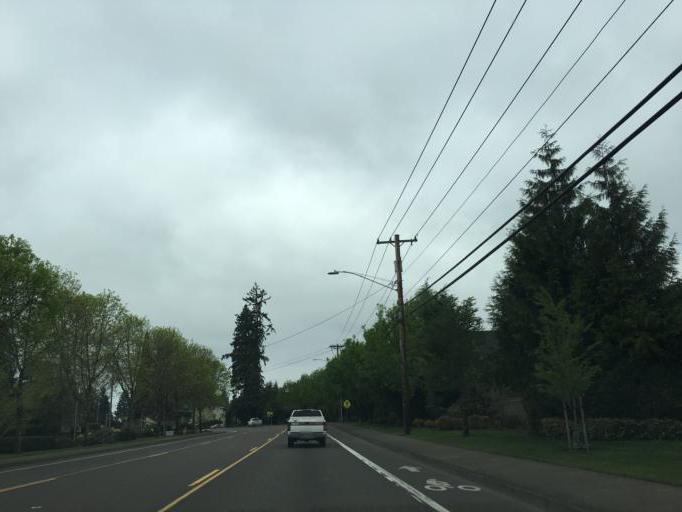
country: US
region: Oregon
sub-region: Washington County
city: Durham
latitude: 45.4037
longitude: -122.7557
